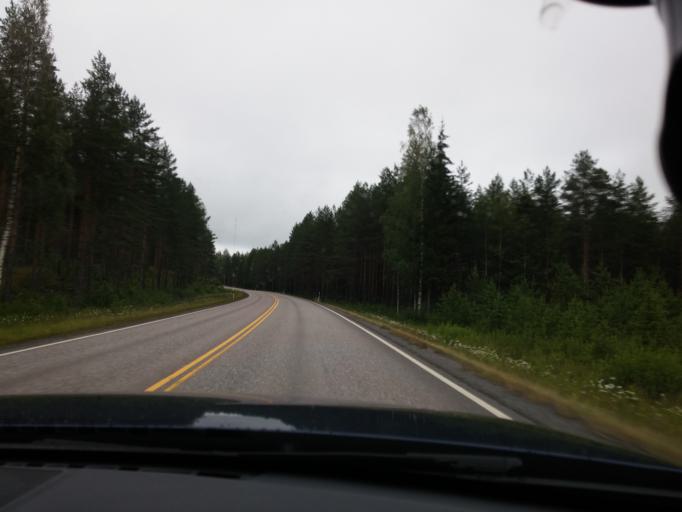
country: FI
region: Pirkanmaa
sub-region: Ylae-Pirkanmaa
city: Vilppula
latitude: 61.9229
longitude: 24.5401
